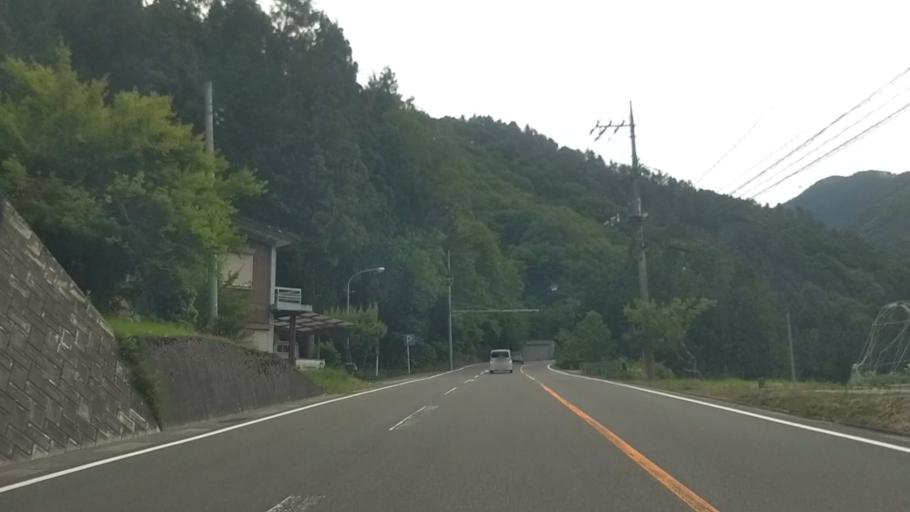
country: JP
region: Yamanashi
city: Fujikawaguchiko
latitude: 35.5277
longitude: 138.6239
